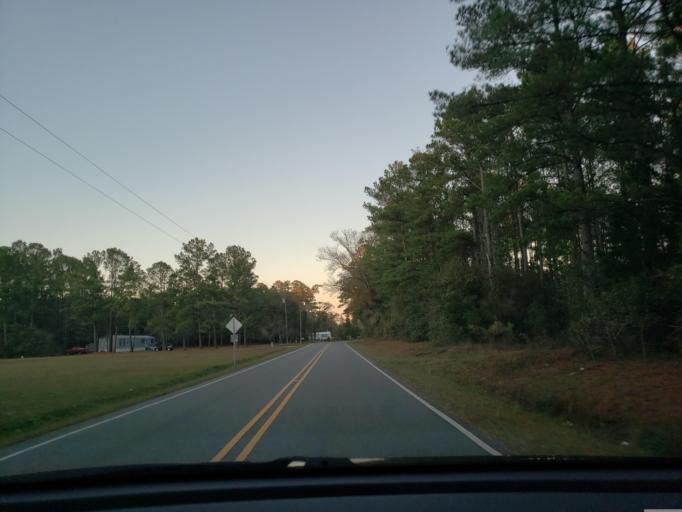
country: US
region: North Carolina
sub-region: Onslow County
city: Richlands
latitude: 34.7283
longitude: -77.6261
